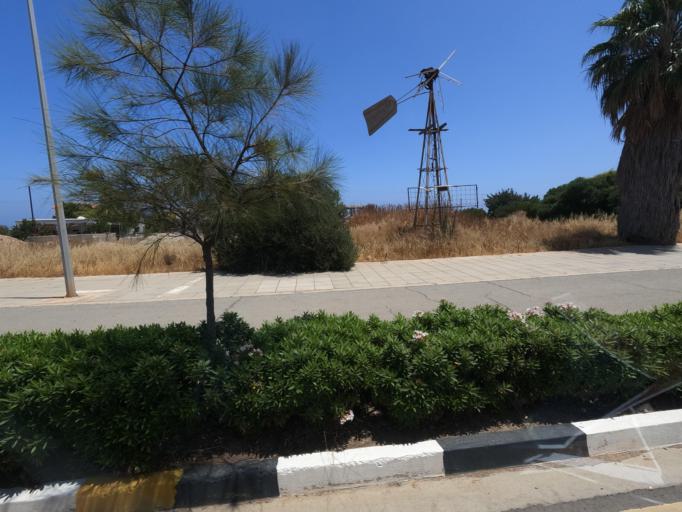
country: CY
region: Ammochostos
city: Paralimni
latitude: 35.0445
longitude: 34.0198
